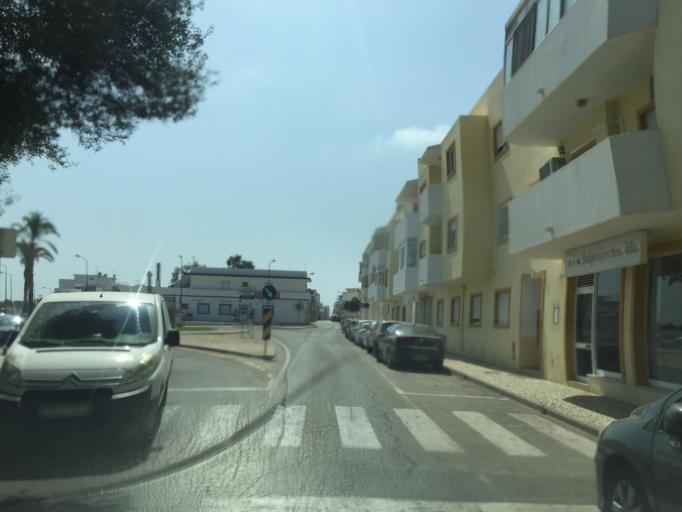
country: PT
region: Faro
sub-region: Olhao
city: Laranjeiro
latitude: 37.0584
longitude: -7.7492
